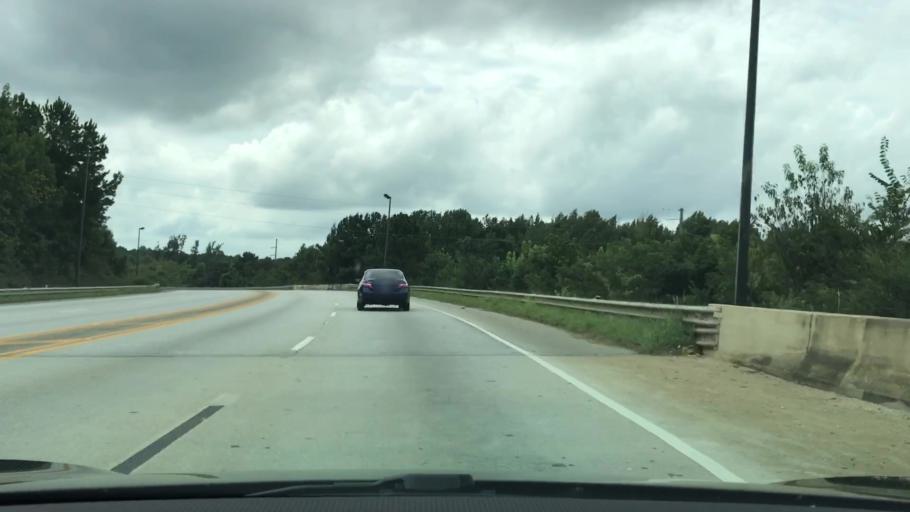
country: US
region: Alabama
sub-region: Lee County
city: Opelika
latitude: 32.6337
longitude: -85.4094
